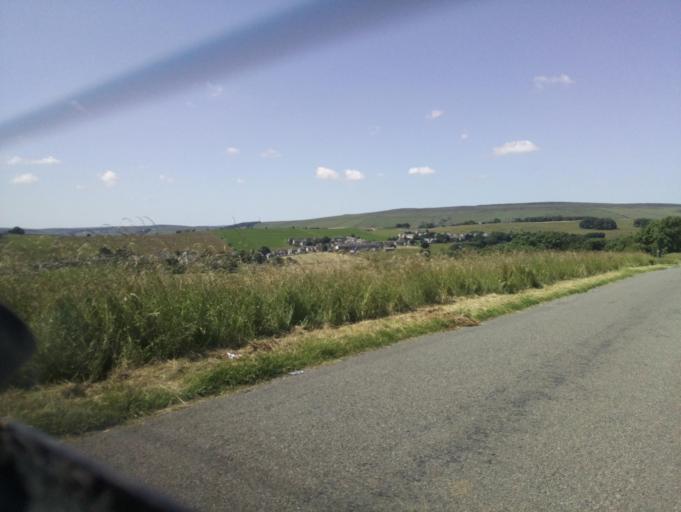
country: GB
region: England
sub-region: Derbyshire
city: Buxton
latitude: 53.2845
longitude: -1.8558
